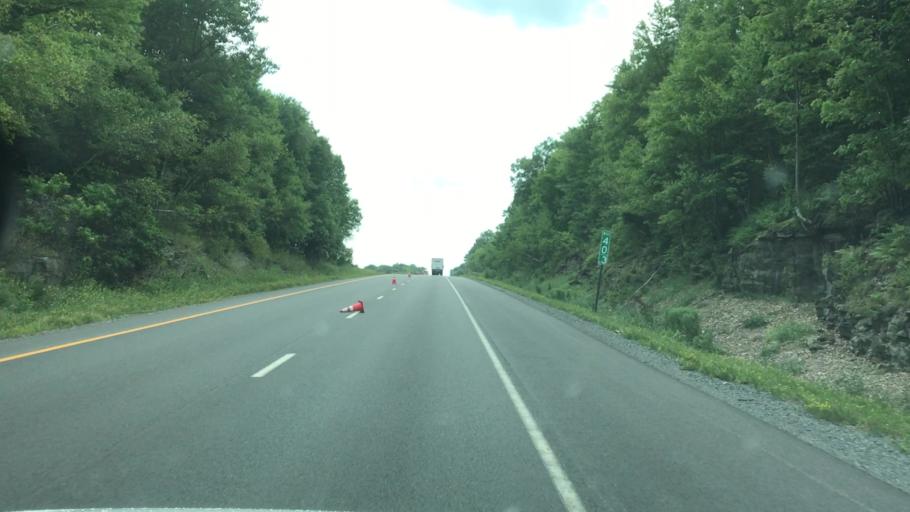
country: US
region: Pennsylvania
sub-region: Pike County
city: Gold Key Lake
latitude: 41.3493
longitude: -74.9464
